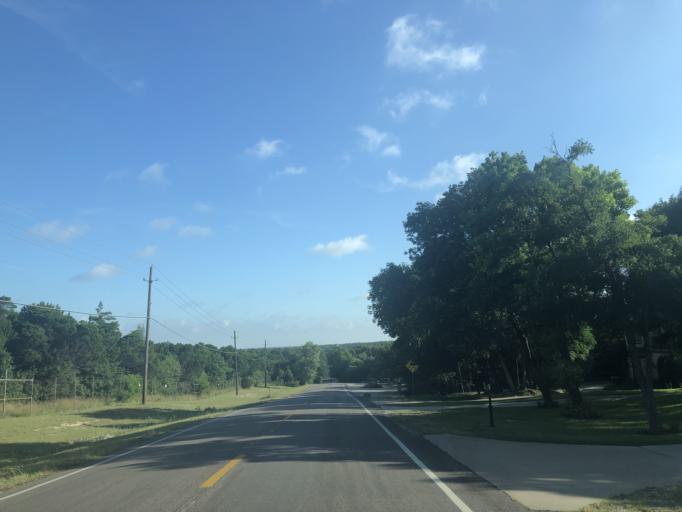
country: US
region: Texas
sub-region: Dallas County
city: Duncanville
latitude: 32.6722
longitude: -96.9256
